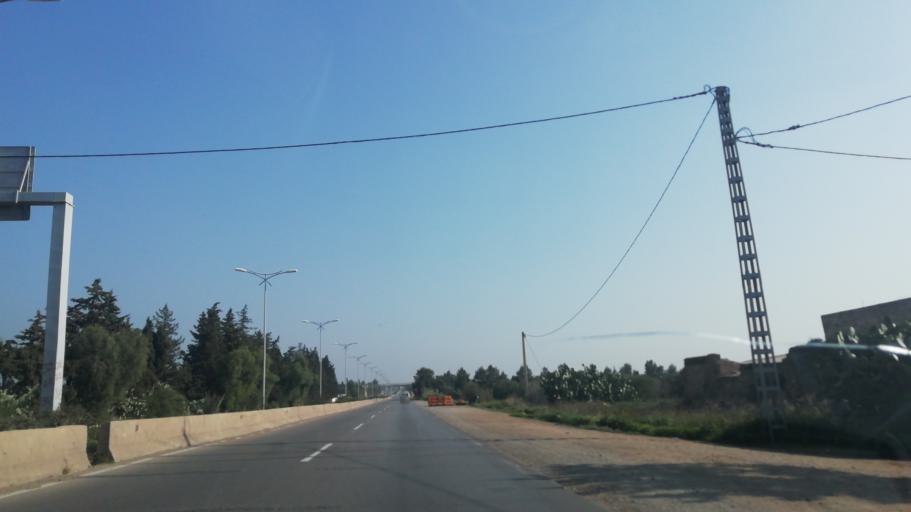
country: DZ
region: Oran
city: Bou Tlelis
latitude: 35.5728
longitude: -0.8737
